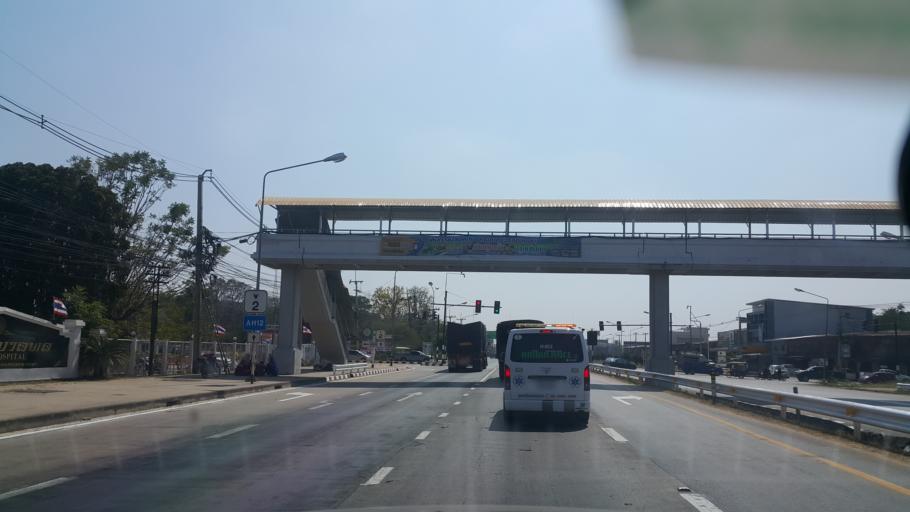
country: TH
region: Khon Kaen
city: Phon
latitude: 15.8166
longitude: 102.6077
